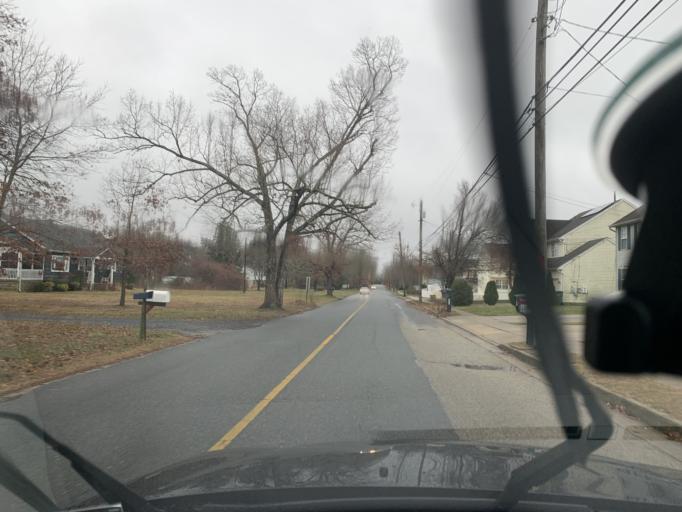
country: US
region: New Jersey
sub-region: Atlantic County
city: Pomona
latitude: 39.4299
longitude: -74.5876
